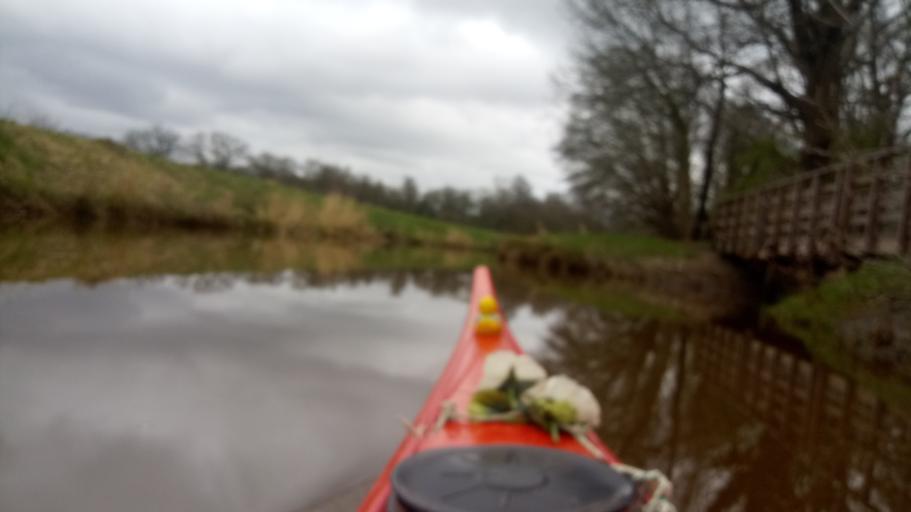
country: NL
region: Groningen
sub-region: Gemeente Vlagtwedde
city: Sellingen
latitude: 52.9430
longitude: 7.1332
